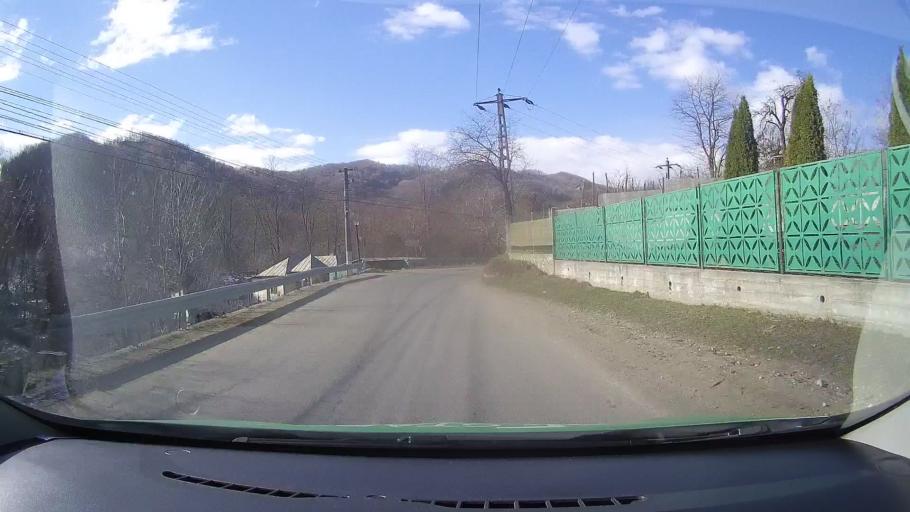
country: RO
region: Dambovita
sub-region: Comuna Varfuri
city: Varfuri
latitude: 45.0871
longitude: 25.4992
